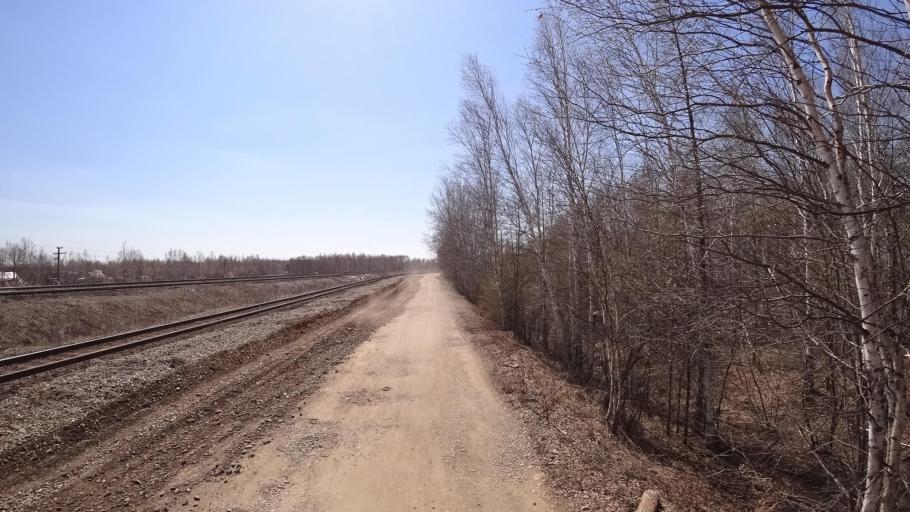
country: RU
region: Khabarovsk Krai
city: Khurba
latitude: 50.4215
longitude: 136.8926
